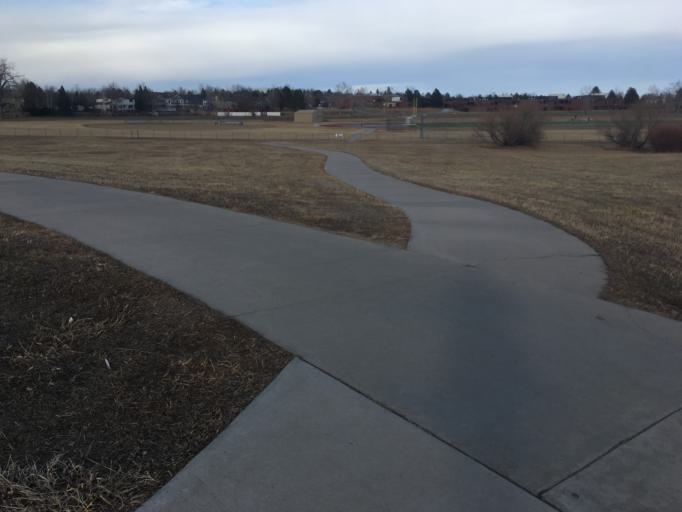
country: US
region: Colorado
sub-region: Broomfield County
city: Broomfield
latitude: 39.9353
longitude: -105.0814
